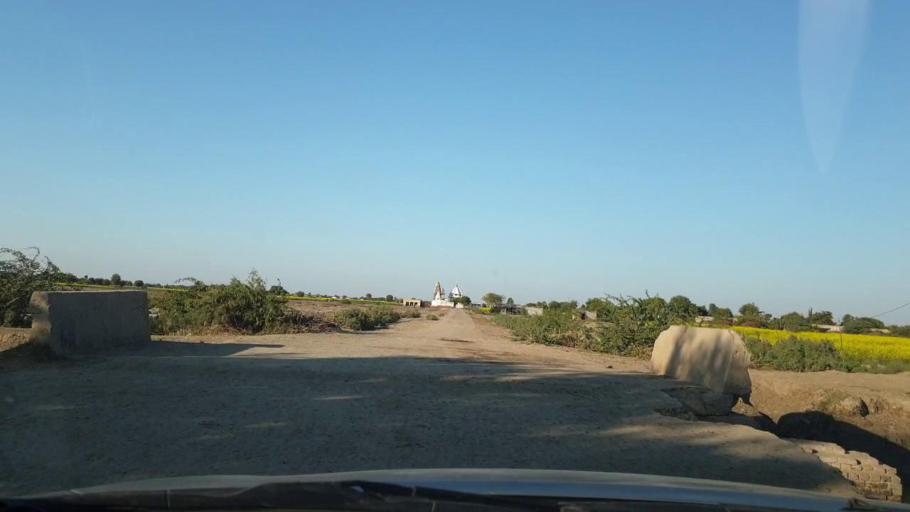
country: PK
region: Sindh
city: Jhol
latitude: 25.9093
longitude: 68.9253
